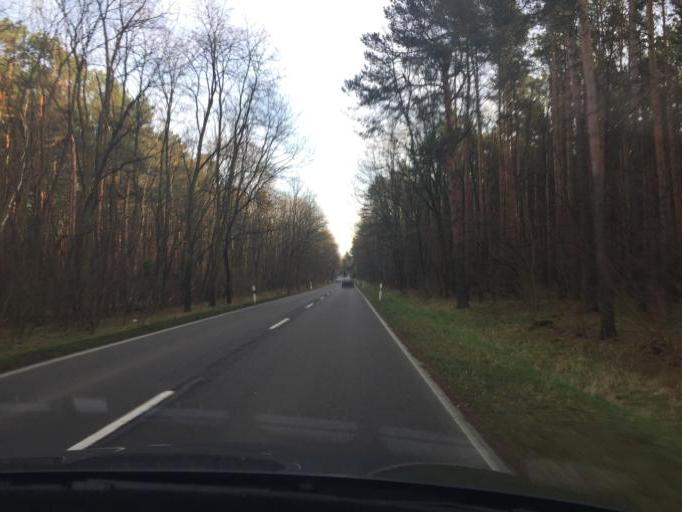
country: DE
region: Brandenburg
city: Forst
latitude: 51.7232
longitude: 14.5579
